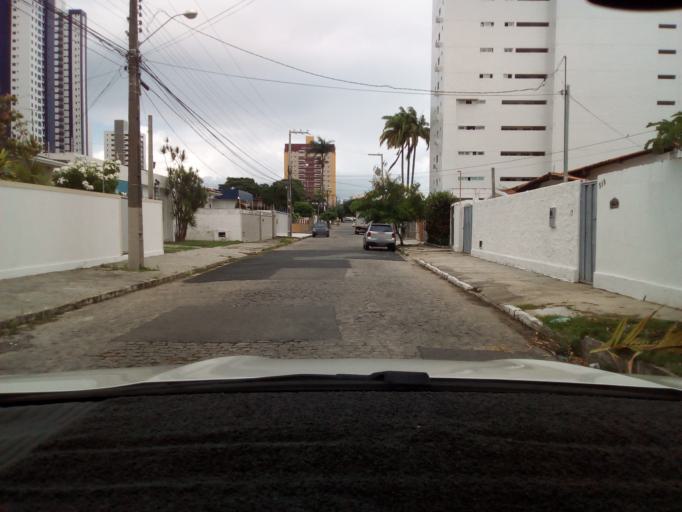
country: BR
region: Paraiba
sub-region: Joao Pessoa
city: Joao Pessoa
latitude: -7.1166
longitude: -34.8566
